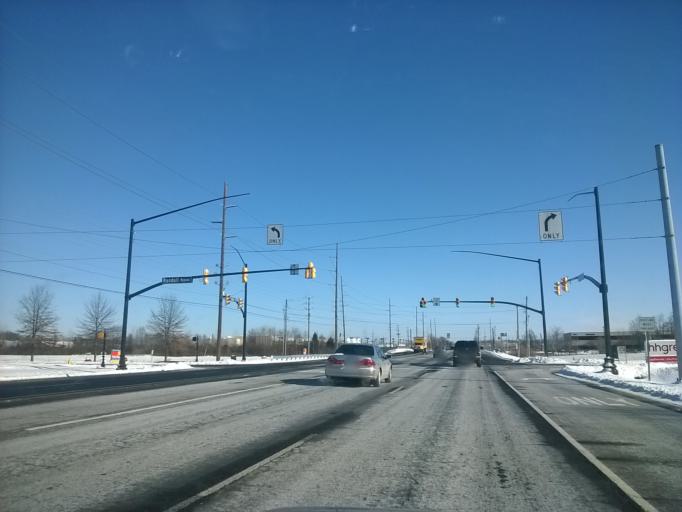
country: US
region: Indiana
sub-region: Hamilton County
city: Carmel
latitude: 39.9268
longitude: -86.0971
